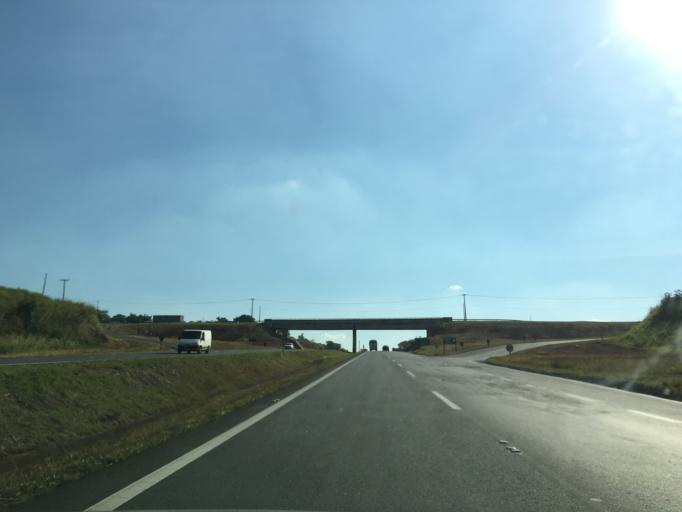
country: BR
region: Sao Paulo
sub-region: Piracicaba
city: Piracicaba
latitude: -22.7241
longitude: -47.5823
